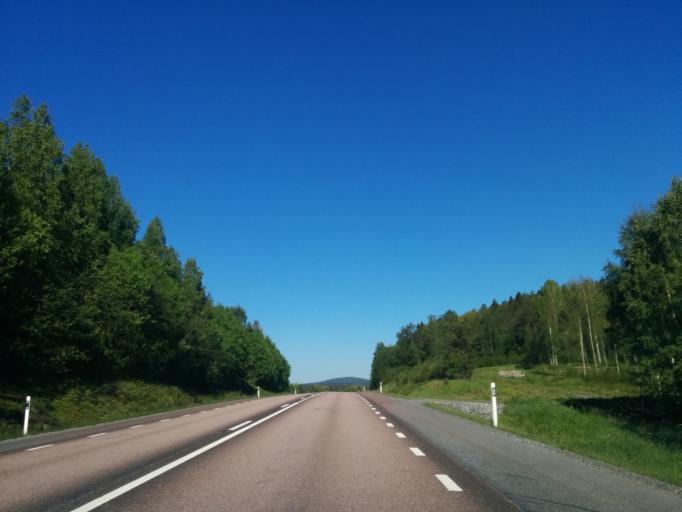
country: SE
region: Vaesternorrland
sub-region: Haernoesands Kommun
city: Haernoesand
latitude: 62.7944
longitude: 17.8941
